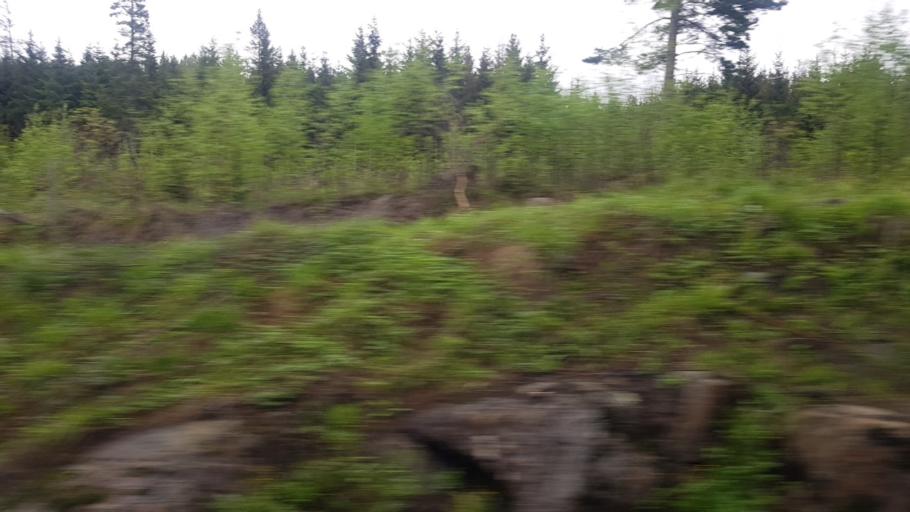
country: NO
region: Oppland
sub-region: Oyer
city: Tretten
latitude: 61.2524
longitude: 10.4267
